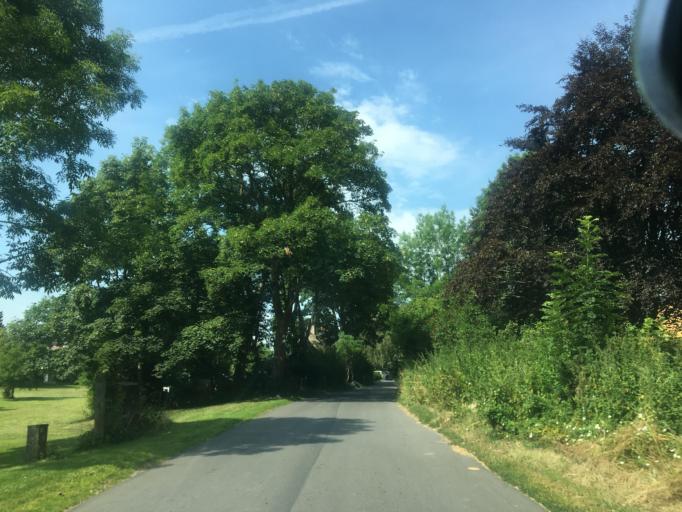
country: DK
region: Zealand
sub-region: Faxe Kommune
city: Ronnede
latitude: 55.2024
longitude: 12.0400
